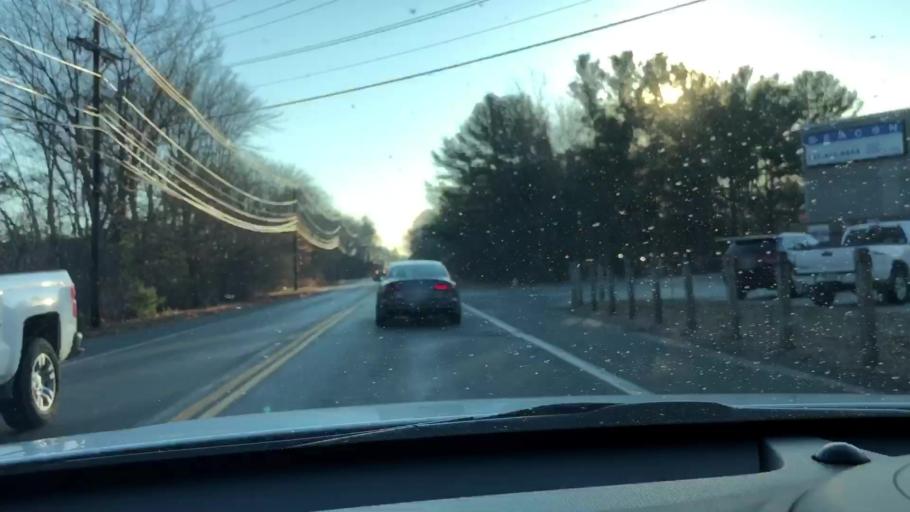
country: US
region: Massachusetts
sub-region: Plymouth County
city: Rockland
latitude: 42.1642
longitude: -70.8901
